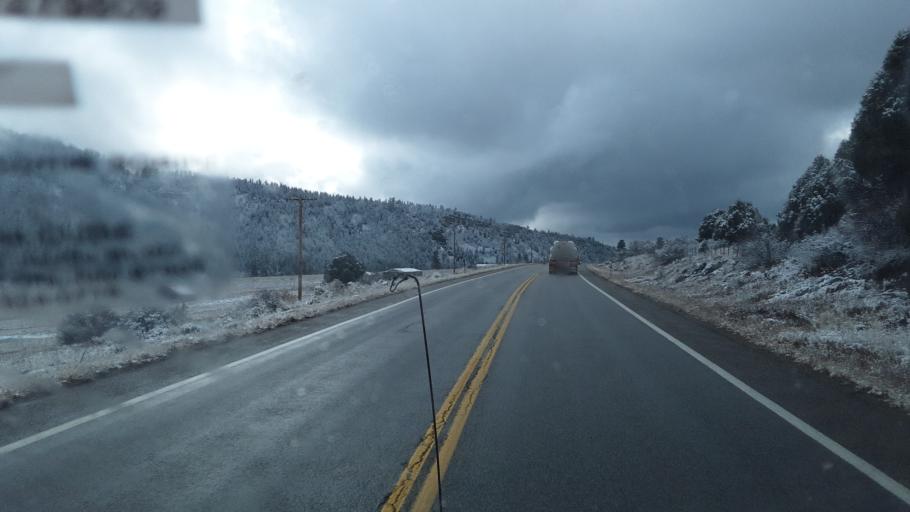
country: US
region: Colorado
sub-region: Archuleta County
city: Pagosa Springs
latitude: 37.2196
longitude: -107.2211
